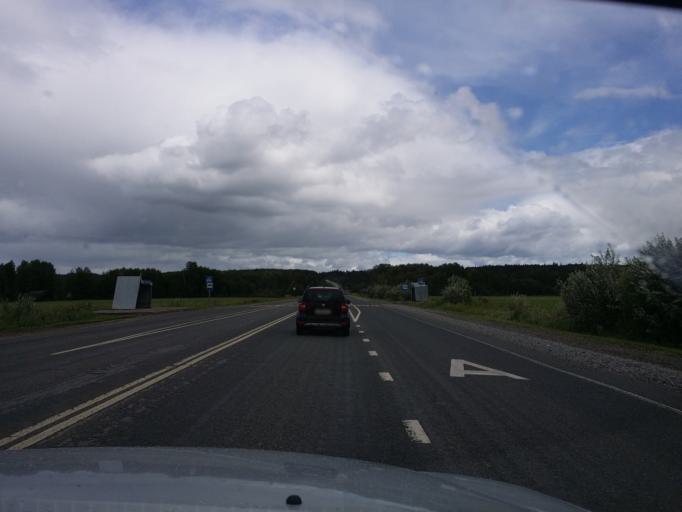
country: RU
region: Tjumen
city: Abalak
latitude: 58.4671
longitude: 68.5292
